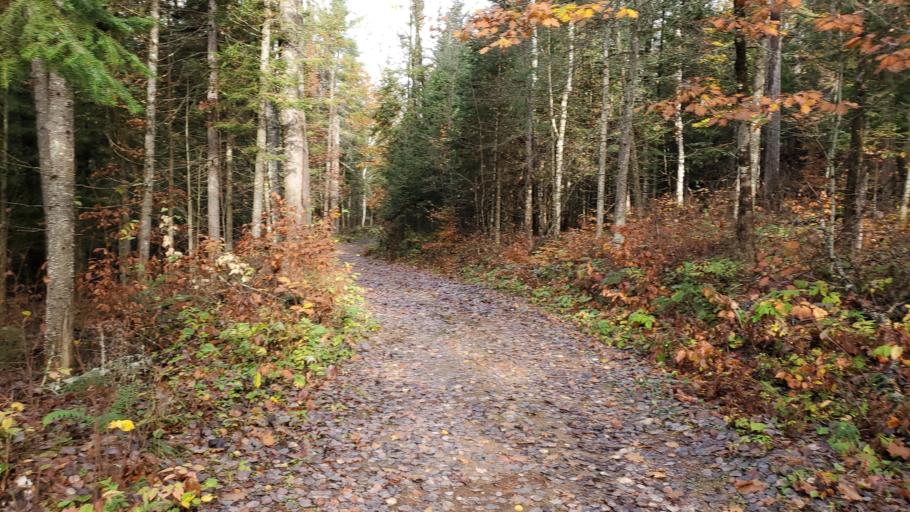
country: CA
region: Ontario
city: Renfrew
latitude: 45.2578
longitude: -77.1849
